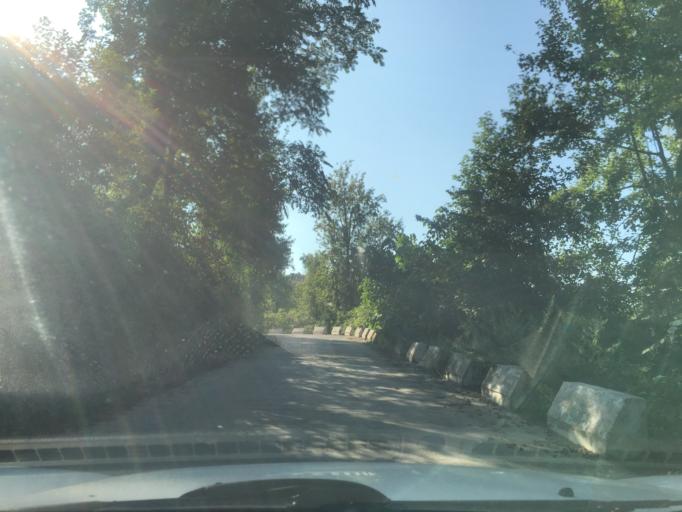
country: CN
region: Guangxi Zhuangzu Zizhiqu
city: Xinzhou
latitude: 25.4396
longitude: 105.7490
